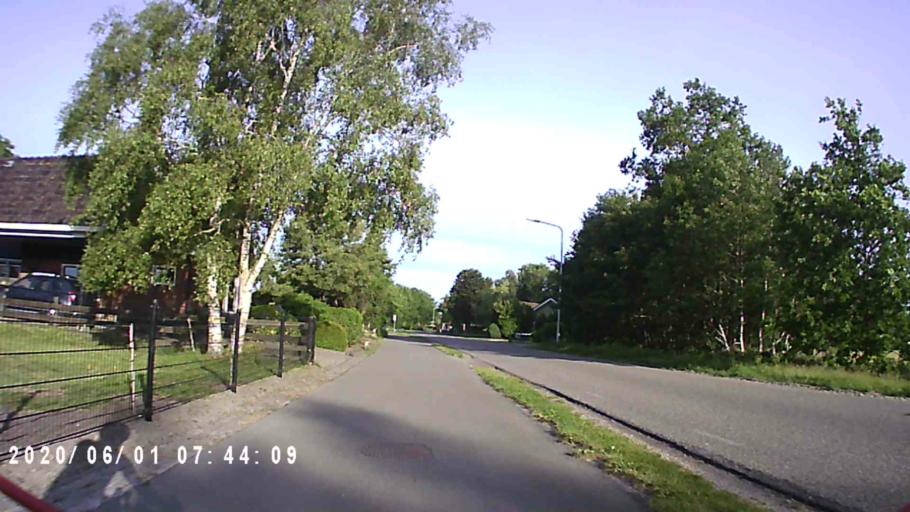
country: NL
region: Friesland
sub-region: Gemeente Dantumadiel
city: Rinsumageast
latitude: 53.2912
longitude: 5.9692
